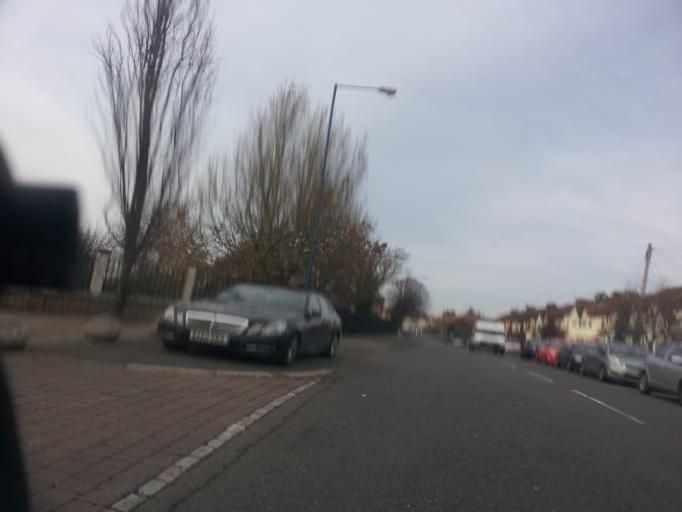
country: GB
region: England
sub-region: Kent
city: Gravesend
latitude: 51.4308
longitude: 0.3645
